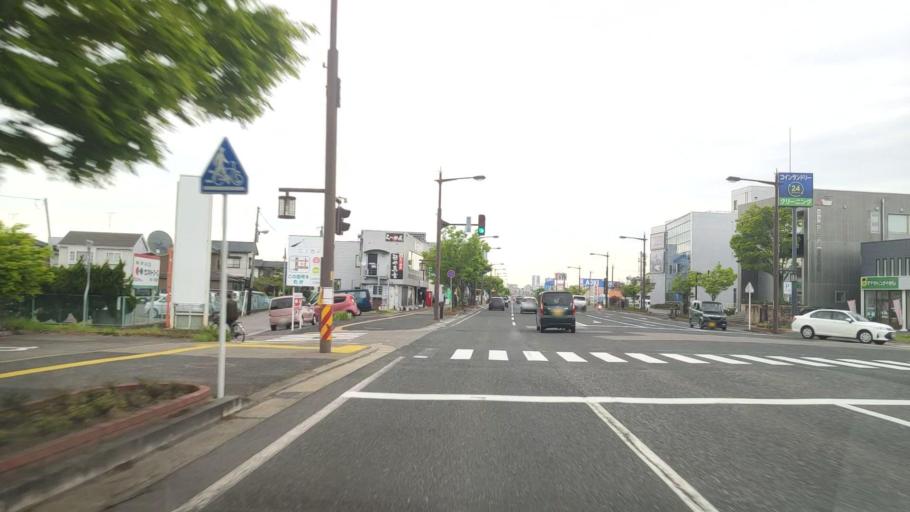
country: JP
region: Niigata
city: Kameda-honcho
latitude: 37.8891
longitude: 139.0705
